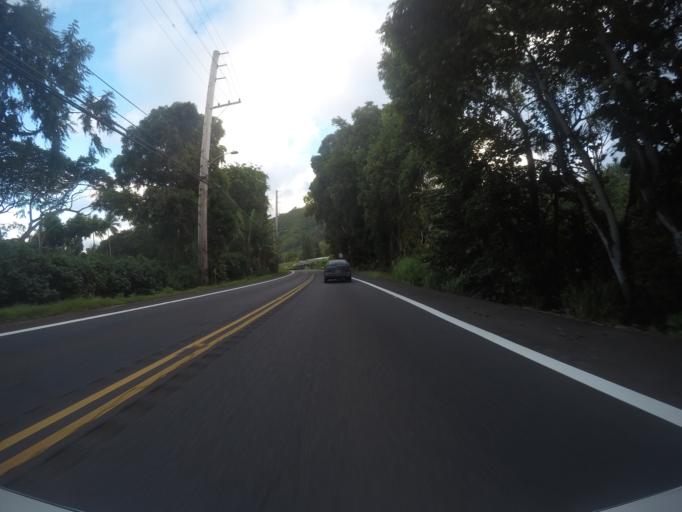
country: US
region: Hawaii
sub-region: Honolulu County
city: Ka'a'awa
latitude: 21.5082
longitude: -157.8554
